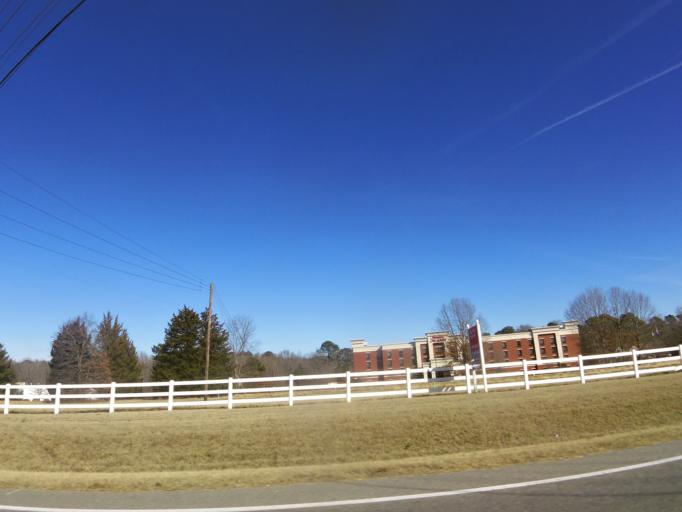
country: US
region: Virginia
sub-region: Isle of Wight County
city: Smithfield
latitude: 36.9603
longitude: -76.6046
